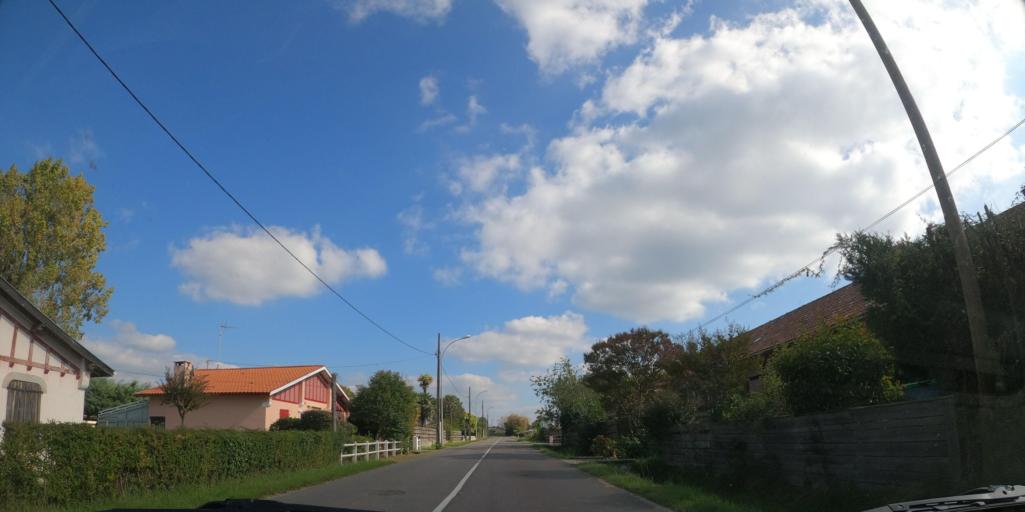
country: FR
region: Aquitaine
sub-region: Departement des Landes
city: Soustons
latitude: 43.7460
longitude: -1.3133
